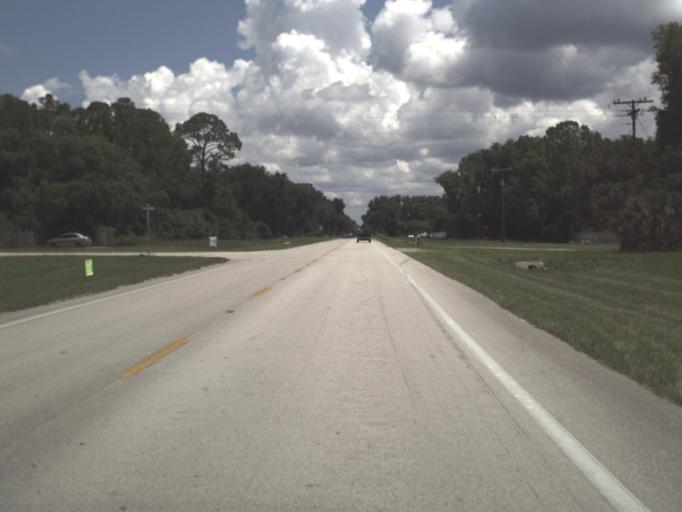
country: US
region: Florida
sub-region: Putnam County
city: Crescent City
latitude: 29.4042
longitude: -81.5094
